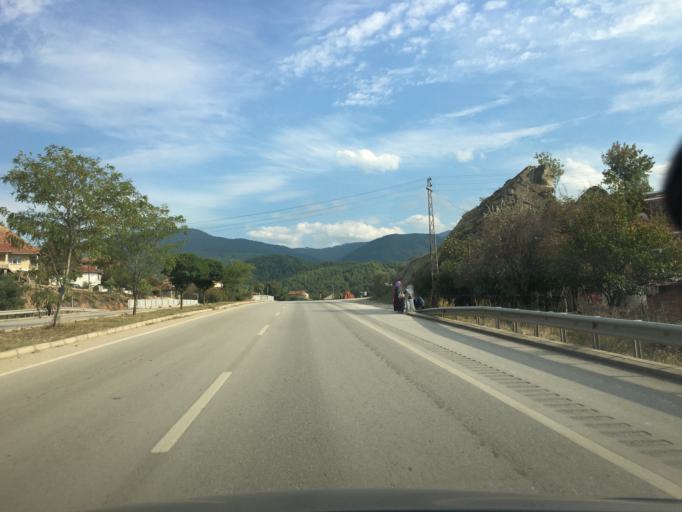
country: TR
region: Karabuk
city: Karabuk
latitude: 41.0971
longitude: 32.6750
